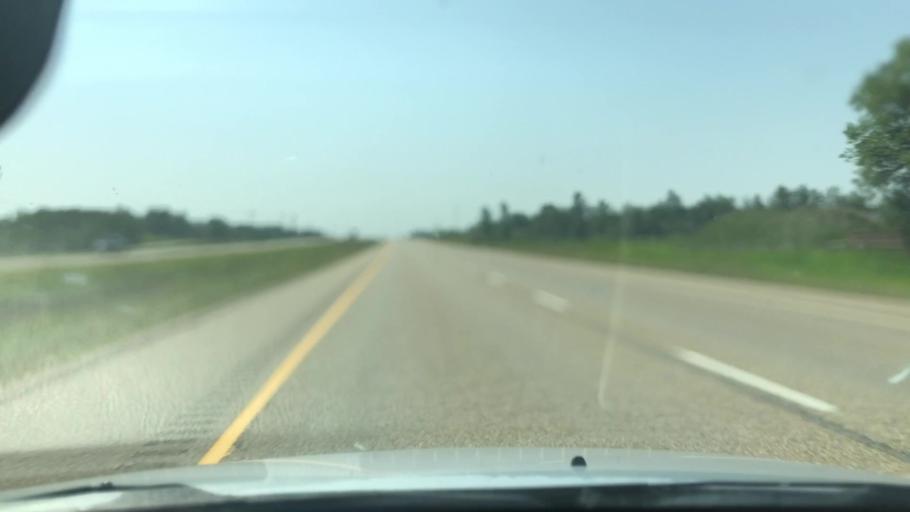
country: CA
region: Alberta
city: Devon
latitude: 53.4441
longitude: -113.7627
